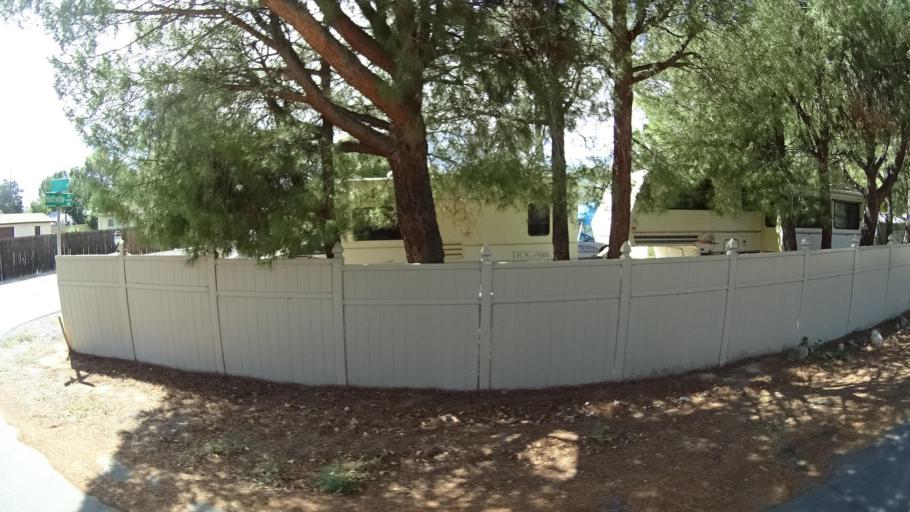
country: MX
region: Baja California
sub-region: Tecate
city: Cereso del Hongo
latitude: 32.6198
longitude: -116.1859
